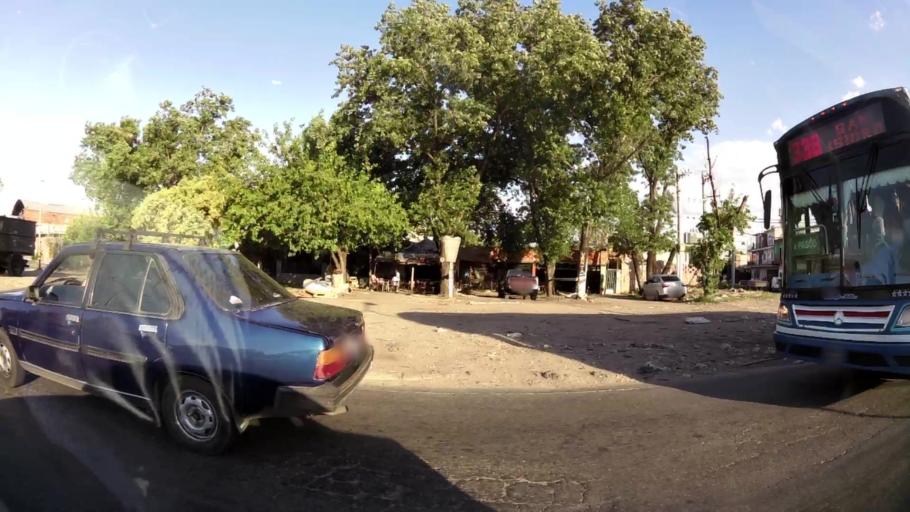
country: AR
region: Buenos Aires
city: Caseros
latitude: -34.5555
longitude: -58.5855
